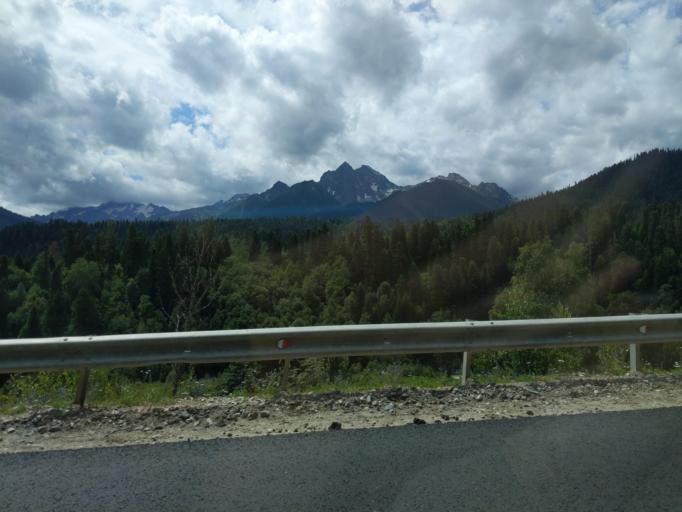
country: RU
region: Karachayevo-Cherkesiya
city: Nizhniy Arkhyz
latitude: 43.5369
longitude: 41.2197
